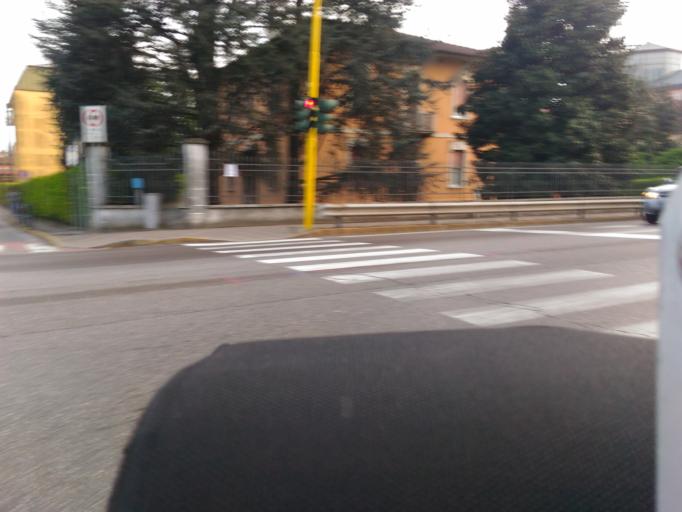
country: IT
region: Lombardy
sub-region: Provincia di Lodi
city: Tavazzano
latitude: 45.3293
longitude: 9.4056
